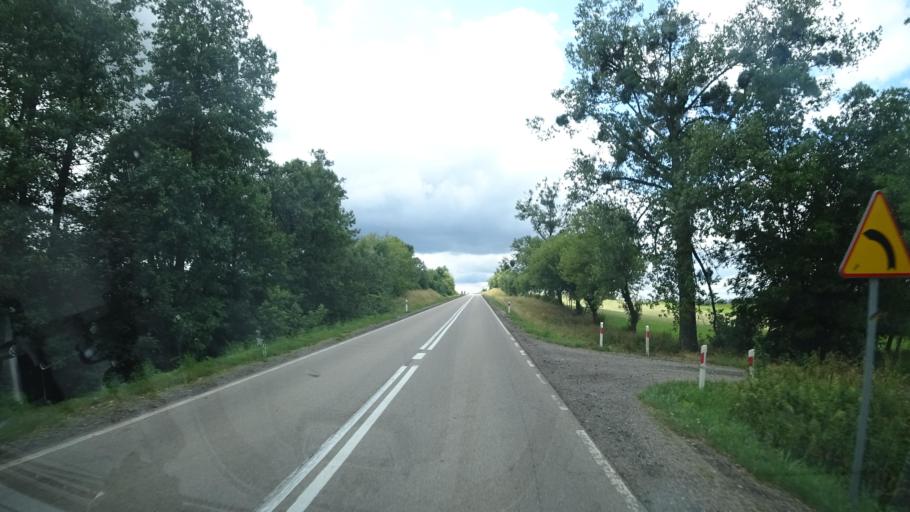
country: PL
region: Warmian-Masurian Voivodeship
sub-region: Powiat goldapski
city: Goldap
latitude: 54.2321
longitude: 22.2498
